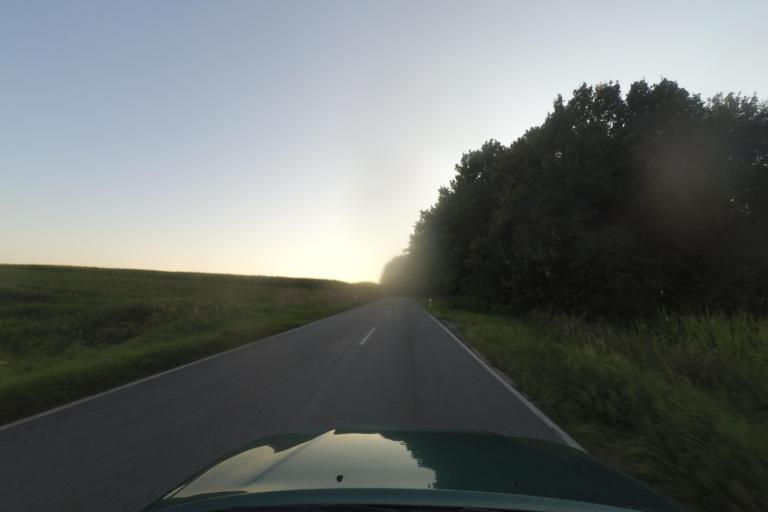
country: DE
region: Bavaria
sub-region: Upper Bavaria
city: Kaufering
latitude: 48.0953
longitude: 10.8975
